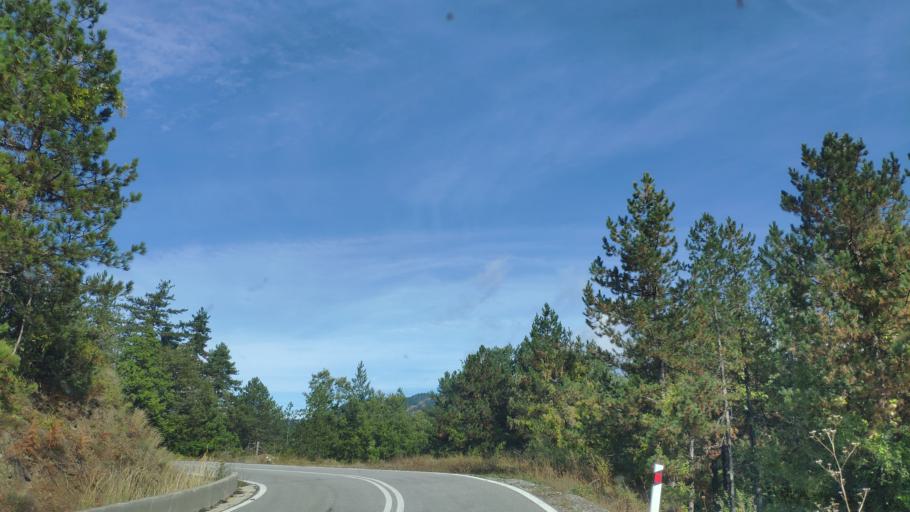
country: AL
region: Korce
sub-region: Rrethi i Devollit
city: Miras
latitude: 40.3754
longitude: 20.9231
